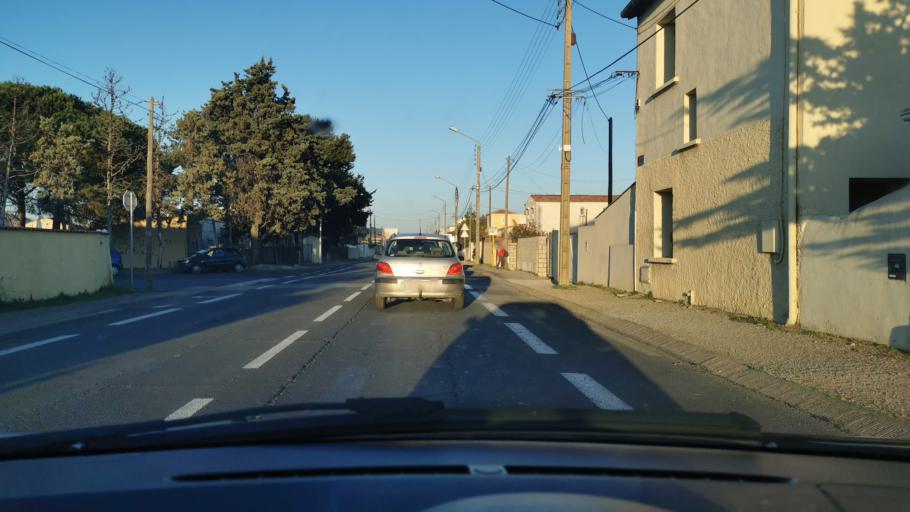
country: FR
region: Languedoc-Roussillon
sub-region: Departement de l'Herault
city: Frontignan
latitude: 43.4407
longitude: 3.7456
